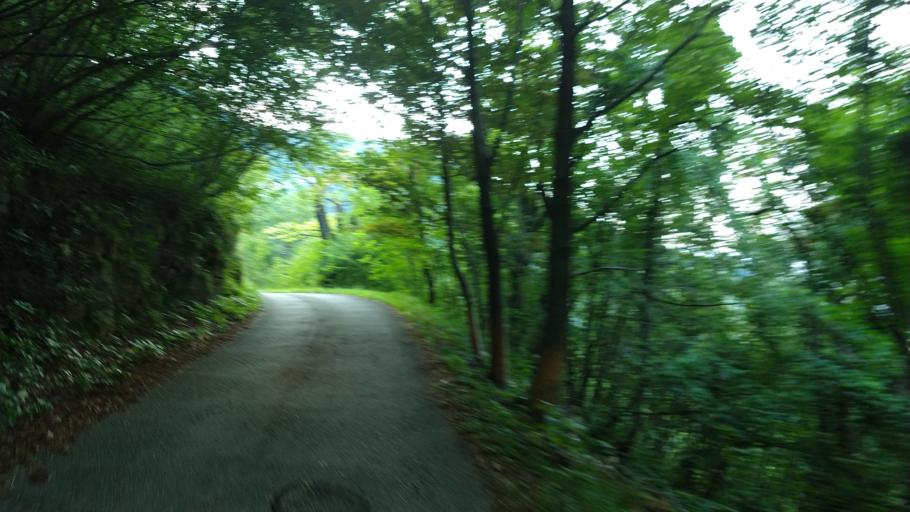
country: IT
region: Veneto
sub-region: Provincia di Vicenza
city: Campolongo sul Brenta
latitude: 45.8260
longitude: 11.6971
